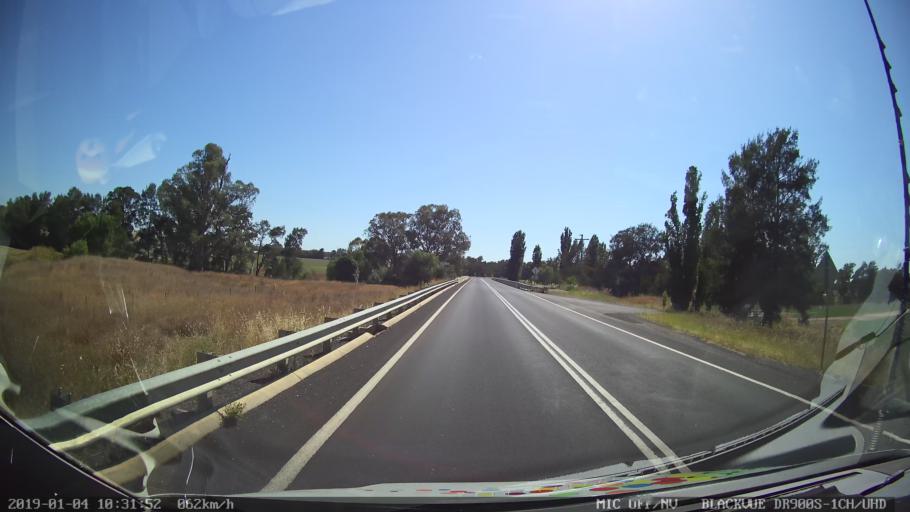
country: AU
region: New South Wales
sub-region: Cabonne
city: Canowindra
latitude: -33.3306
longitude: 148.6341
